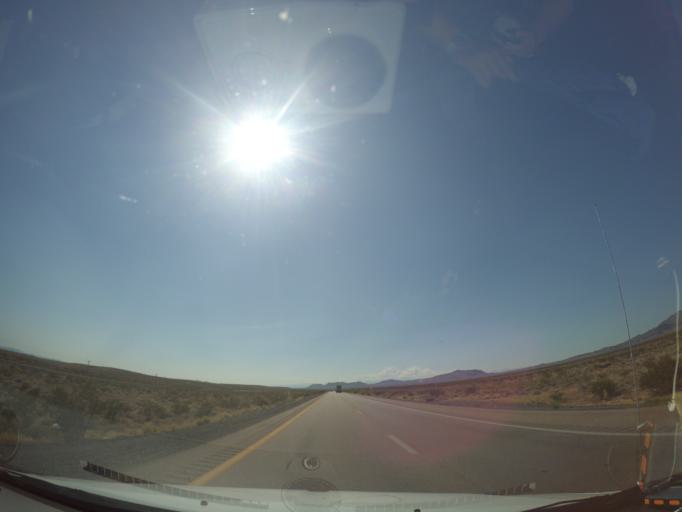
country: US
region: Nevada
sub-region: Clark County
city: Moapa Valley
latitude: 36.7597
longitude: -114.3700
